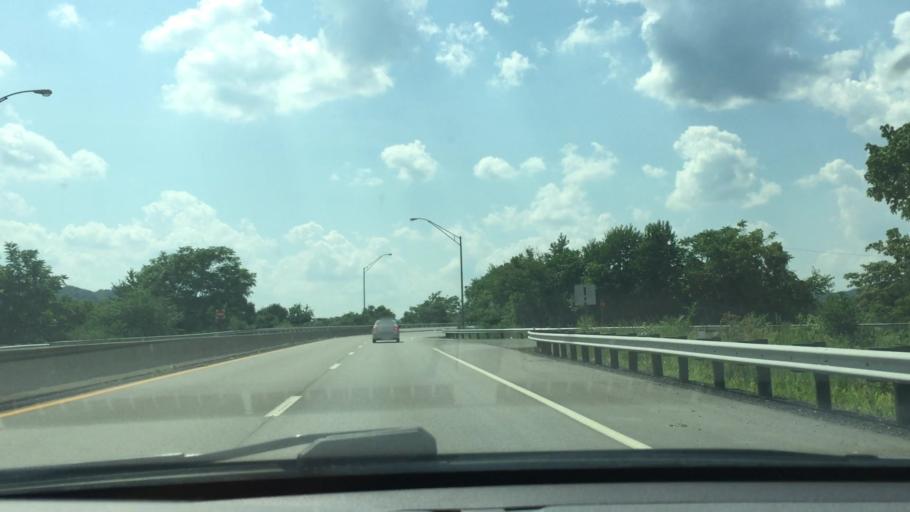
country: US
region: West Virginia
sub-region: Marshall County
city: Moundsville
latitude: 39.9143
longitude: -80.7598
